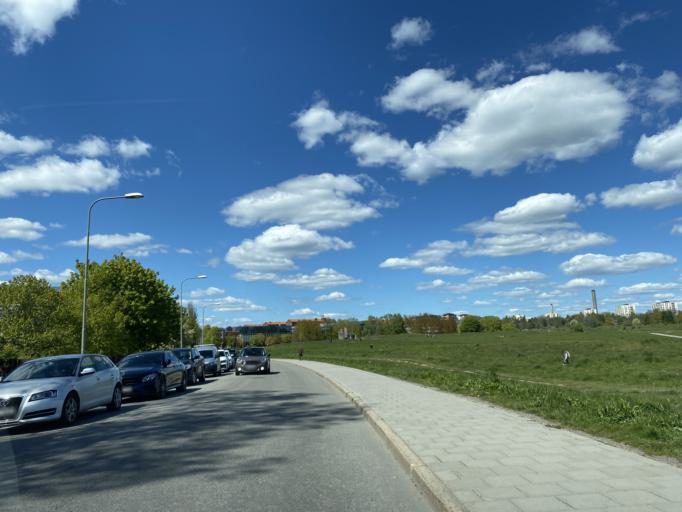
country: SE
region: Stockholm
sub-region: Stockholms Kommun
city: OEstermalm
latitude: 59.3362
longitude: 18.1069
